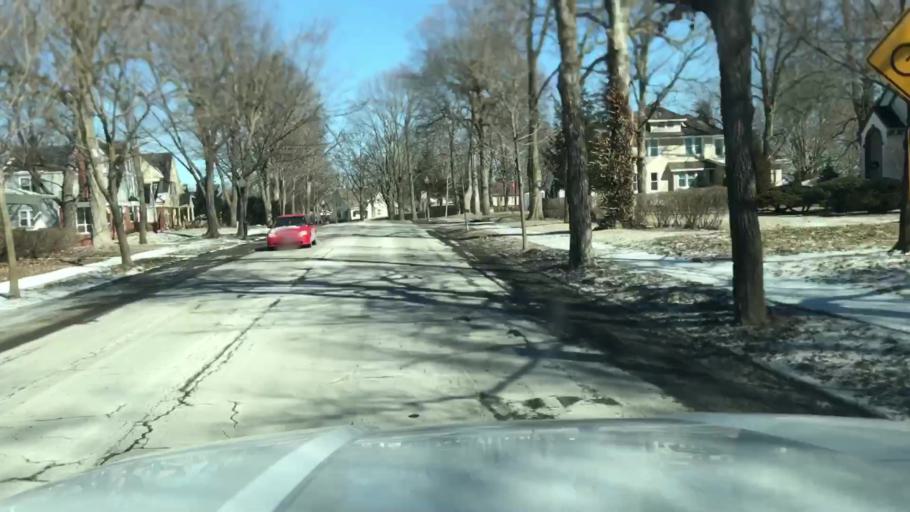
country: US
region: Missouri
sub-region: Buchanan County
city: Saint Joseph
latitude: 39.7832
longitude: -94.8233
